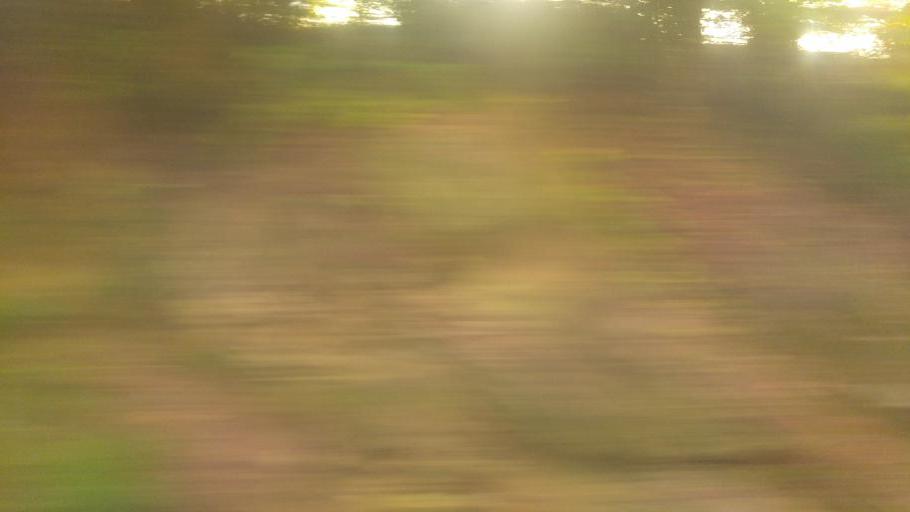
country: US
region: North Carolina
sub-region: Wake County
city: Raleigh
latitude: 35.7704
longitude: -78.6418
